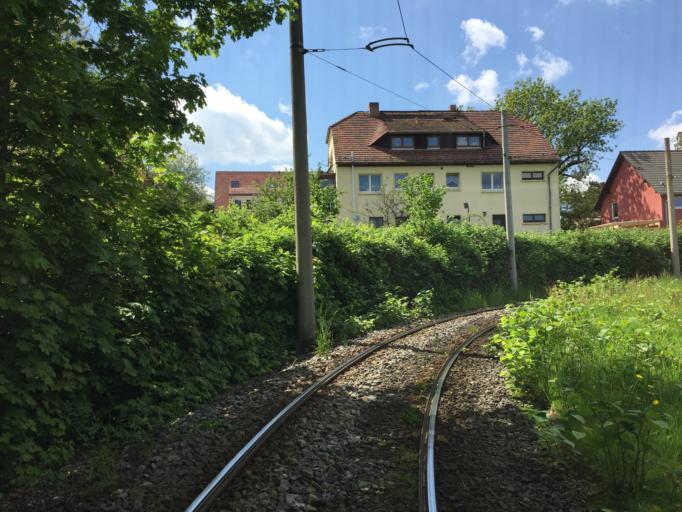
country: DE
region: Saxony
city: Radebeul
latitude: 51.0584
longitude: 13.6702
